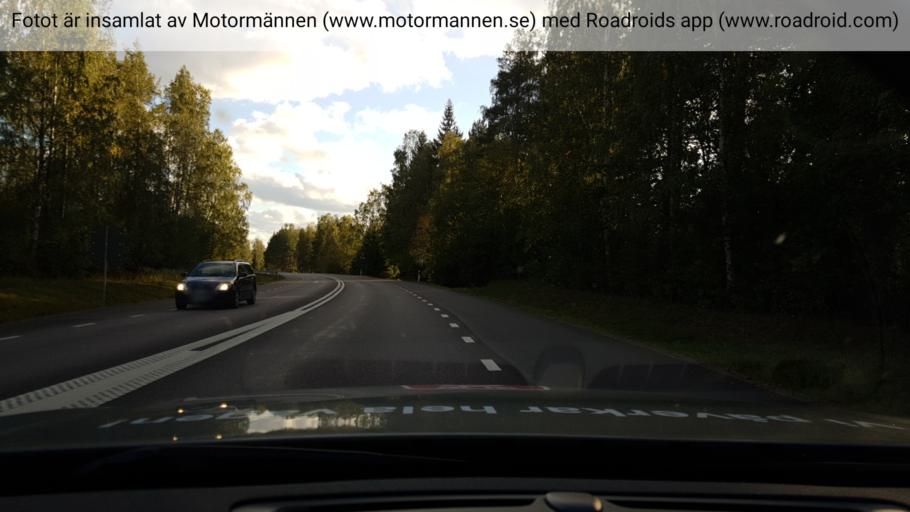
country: SE
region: Vaermland
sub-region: Karlstads Kommun
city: Molkom
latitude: 59.6028
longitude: 13.7390
